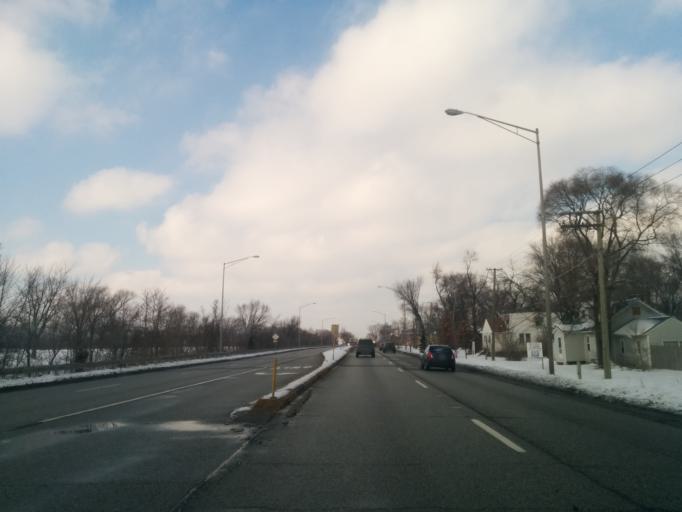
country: US
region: Illinois
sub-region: Cook County
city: Tinley Park
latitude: 41.5660
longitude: -87.7929
